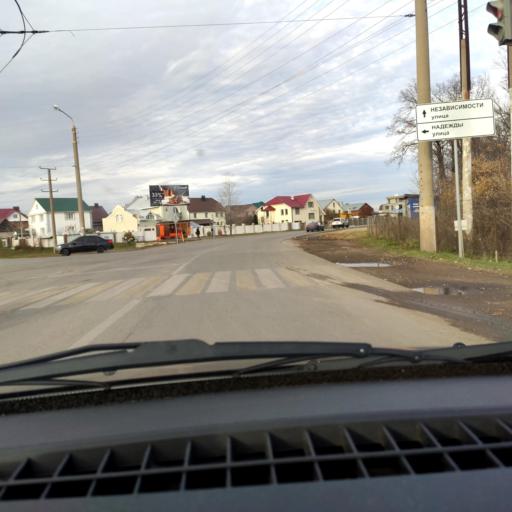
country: RU
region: Bashkortostan
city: Ufa
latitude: 54.7890
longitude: 55.9498
